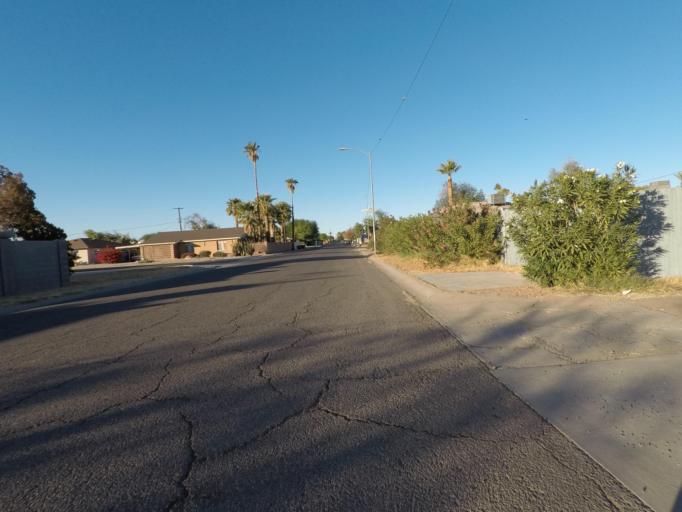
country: US
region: Arizona
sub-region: Maricopa County
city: Phoenix
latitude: 33.4852
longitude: -112.1063
